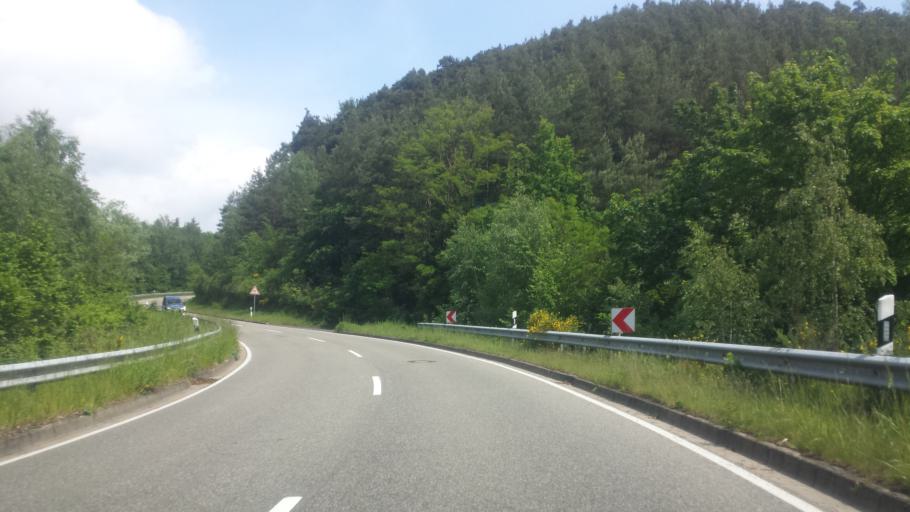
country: DE
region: Rheinland-Pfalz
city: Lindenberg
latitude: 49.3808
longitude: 8.1020
